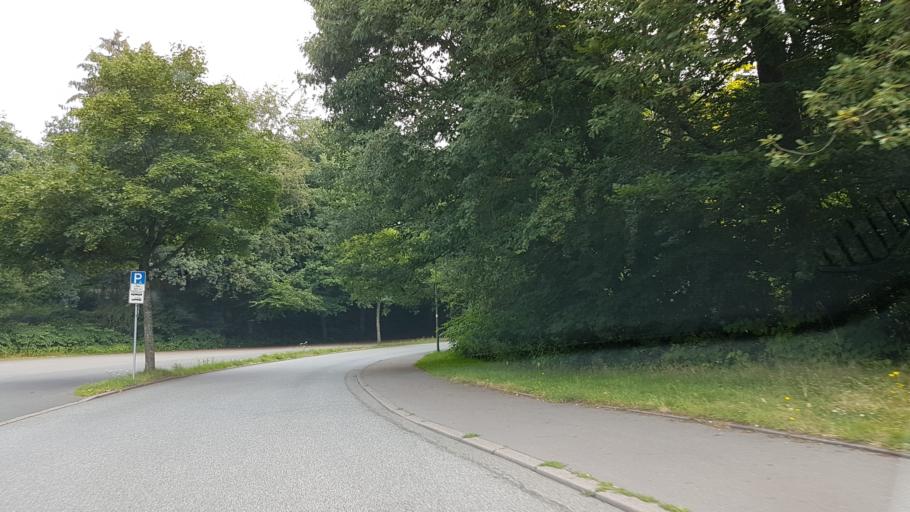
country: DE
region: Saarland
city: Neunkirchen
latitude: 49.3416
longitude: 7.2059
